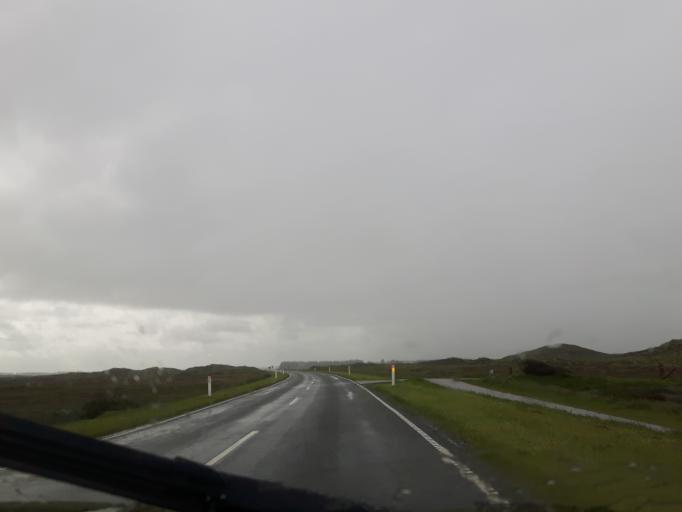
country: DK
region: North Denmark
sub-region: Thisted Kommune
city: Hanstholm
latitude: 57.0188
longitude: 8.4725
